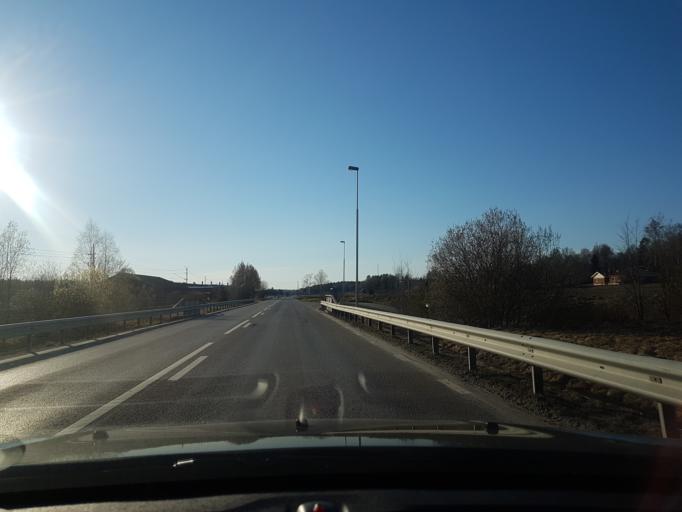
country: SE
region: Uppsala
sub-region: Heby Kommun
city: Morgongava
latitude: 59.9049
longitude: 17.0536
